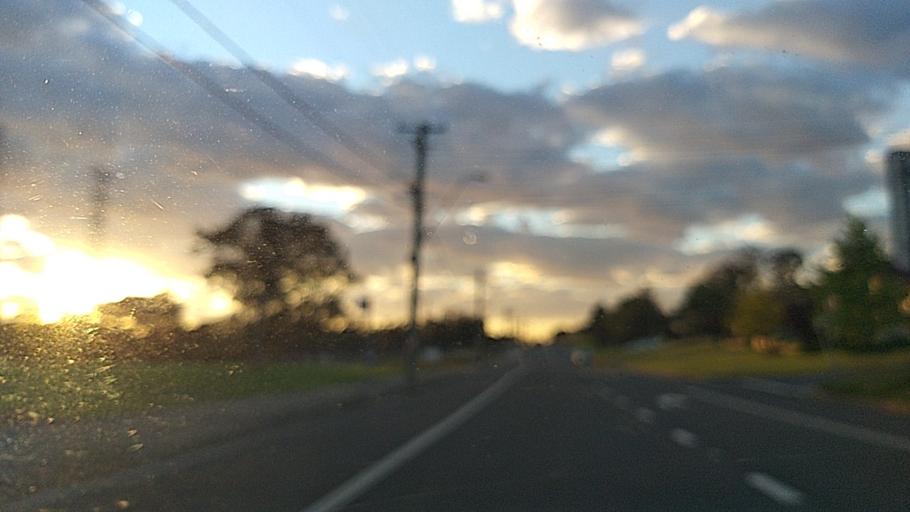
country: AU
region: New South Wales
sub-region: Wollongong
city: Koonawarra
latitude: -34.4894
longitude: 150.8109
